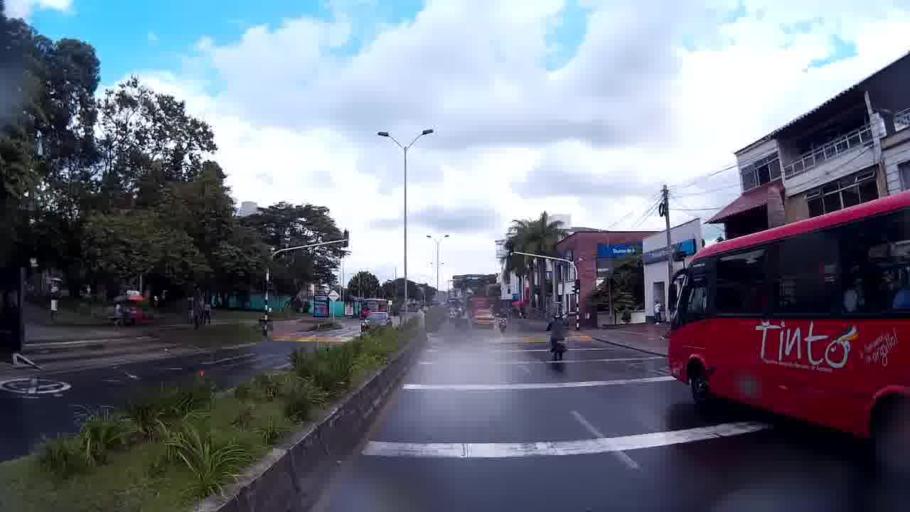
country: CO
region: Quindio
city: Armenia
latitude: 4.5459
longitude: -75.6624
